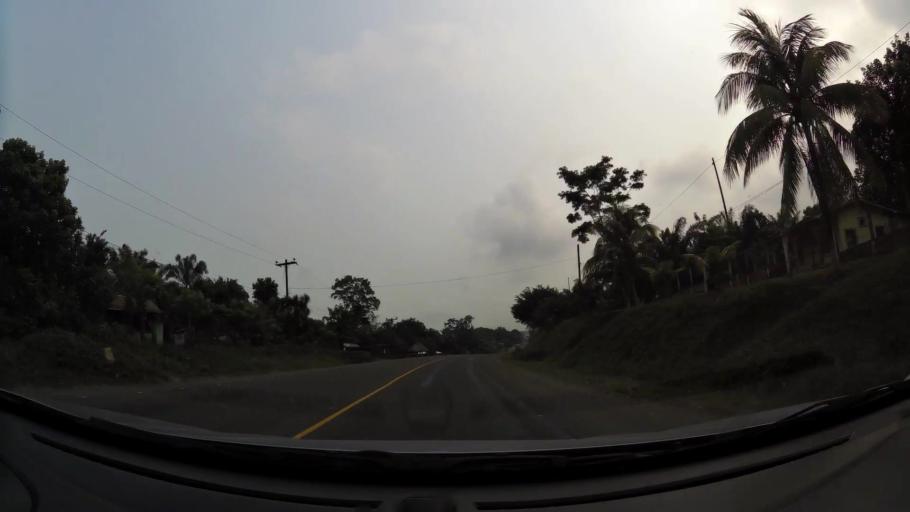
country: HN
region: Atlantida
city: Mezapa
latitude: 15.5709
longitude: -87.6183
